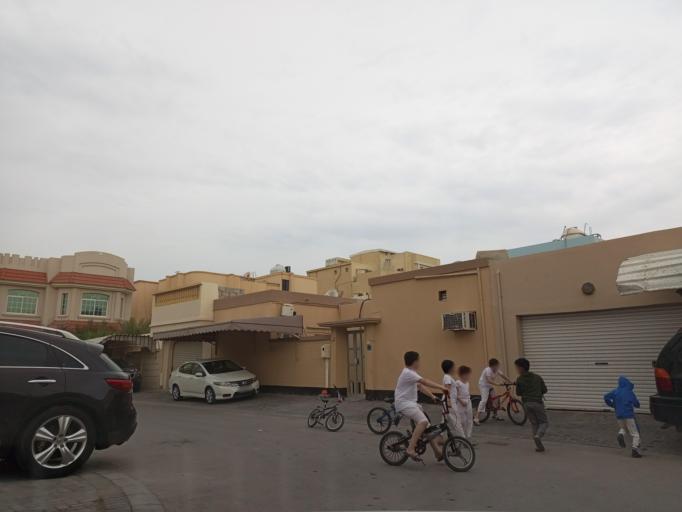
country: BH
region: Muharraq
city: Al Muharraq
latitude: 26.2605
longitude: 50.6340
